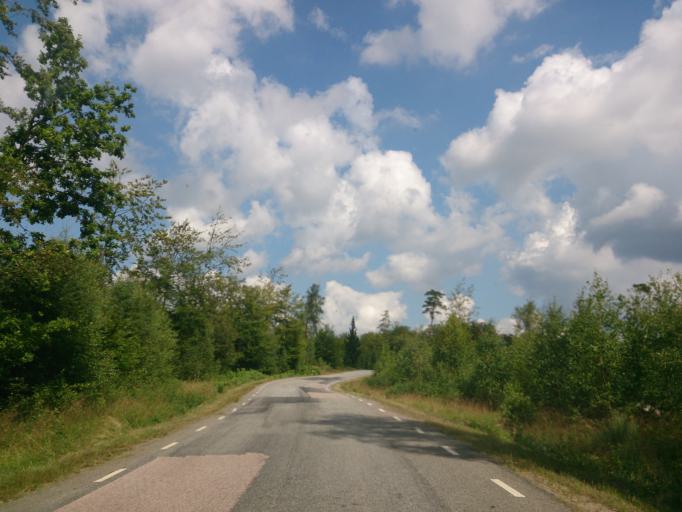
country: SE
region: Joenkoeping
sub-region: Varnamo Kommun
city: Forsheda
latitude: 57.1337
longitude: 13.8741
